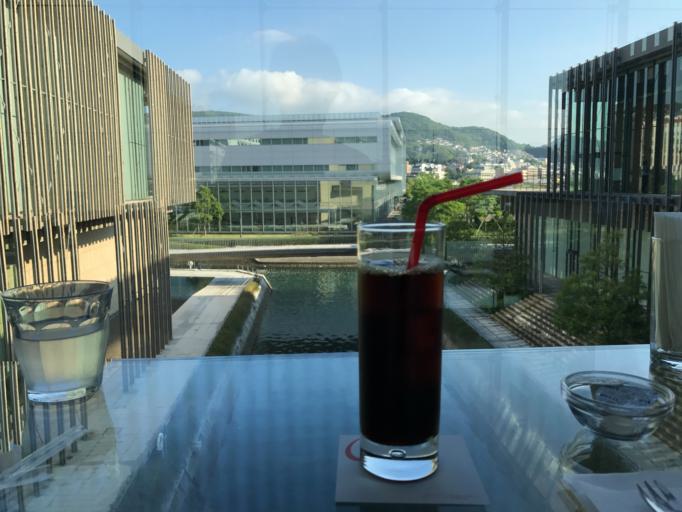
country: JP
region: Nagasaki
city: Nagasaki-shi
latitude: 32.7417
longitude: 129.8709
